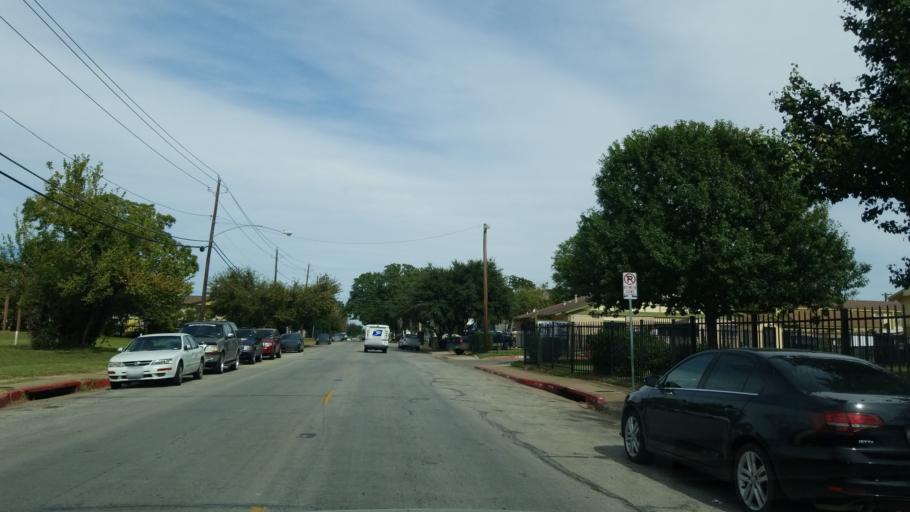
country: US
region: Texas
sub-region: Dallas County
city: Dallas
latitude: 32.7610
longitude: -96.7388
